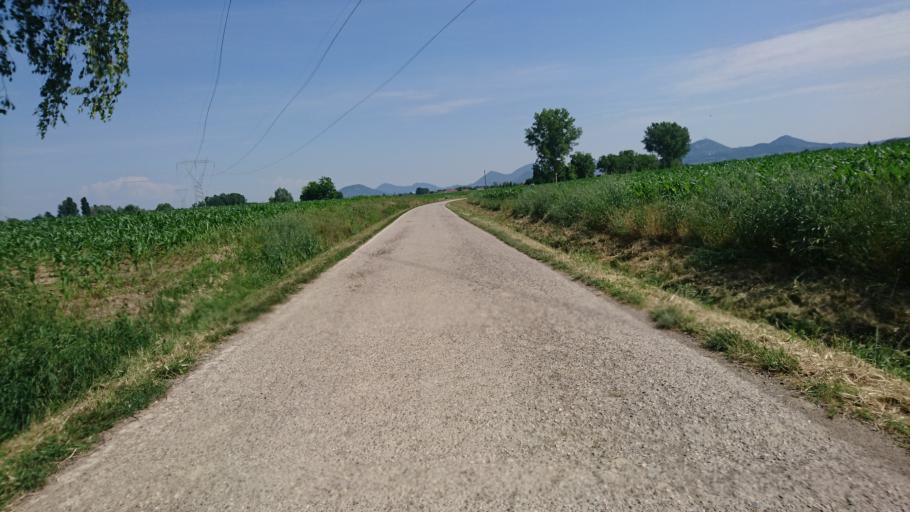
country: IT
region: Veneto
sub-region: Provincia di Padova
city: Ospedaletto Euganeo
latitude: 45.2036
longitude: 11.5890
